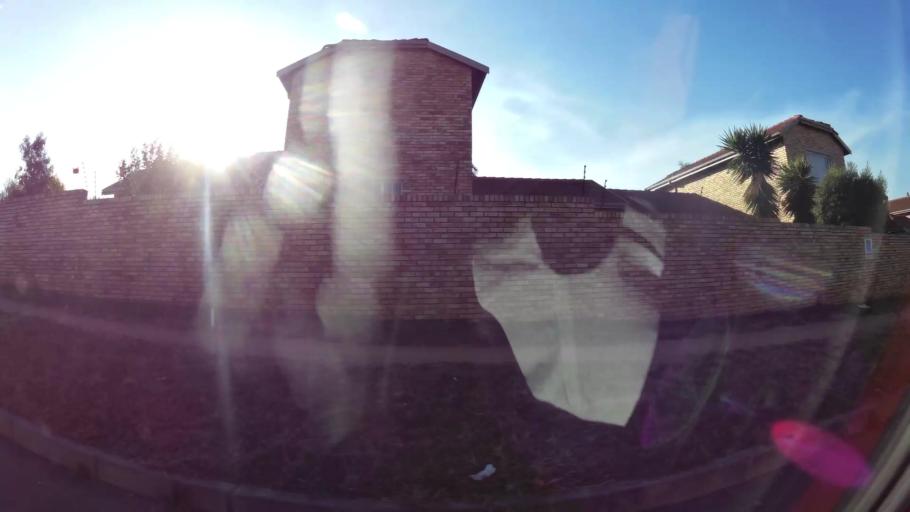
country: ZA
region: Gauteng
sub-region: City of Johannesburg Metropolitan Municipality
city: Roodepoort
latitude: -26.0792
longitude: 27.9489
